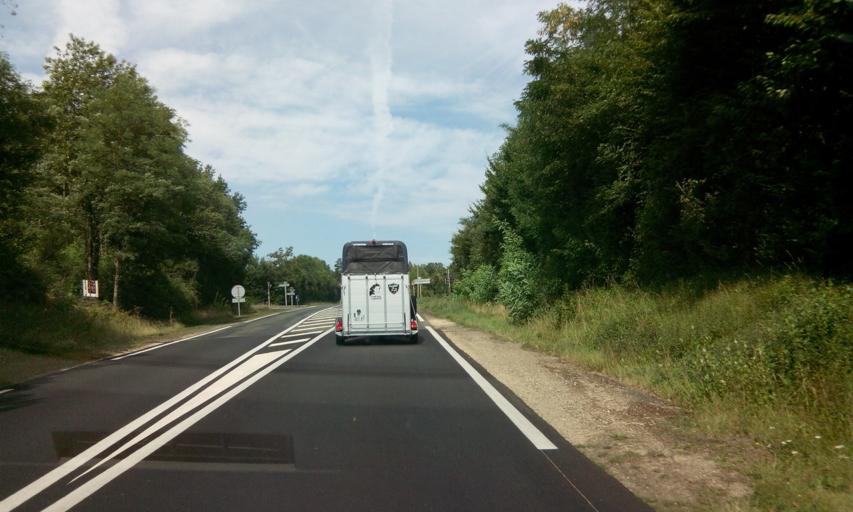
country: FR
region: Poitou-Charentes
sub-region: Departement des Deux-Sevres
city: Sauze-Vaussais
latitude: 46.1509
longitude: 0.0620
